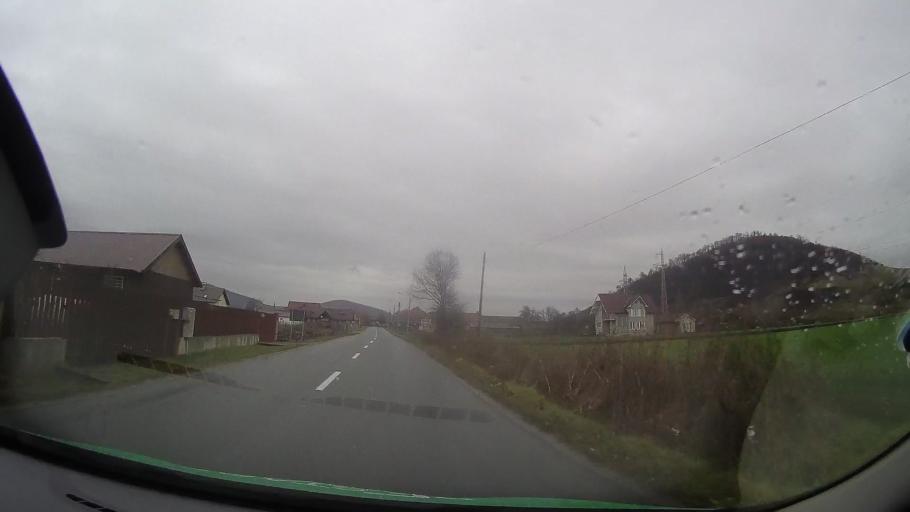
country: RO
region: Bistrita-Nasaud
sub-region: Municipiul Bistrita
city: Viisoara
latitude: 47.0665
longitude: 24.4374
